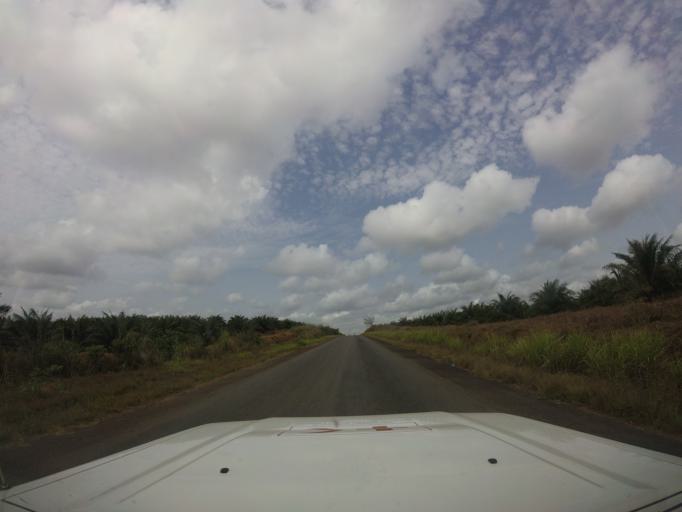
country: LR
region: Bomi
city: Tubmanburg
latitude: 6.7284
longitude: -11.0280
